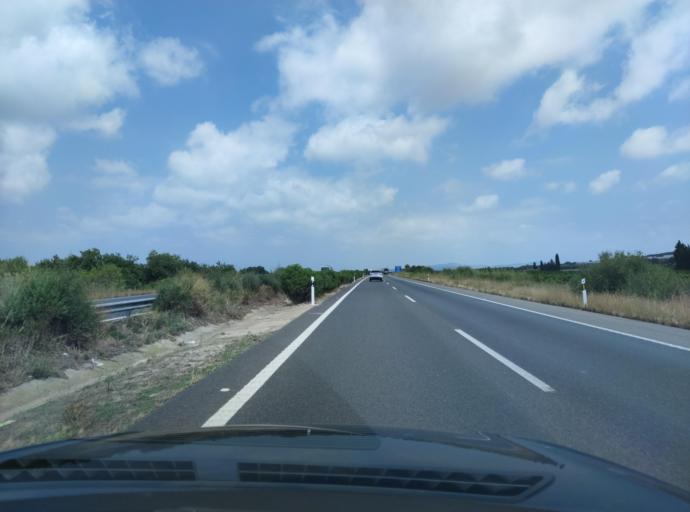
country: ES
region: Valencia
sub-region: Provincia de Castello
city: Vinaros
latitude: 40.5076
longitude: 0.4156
